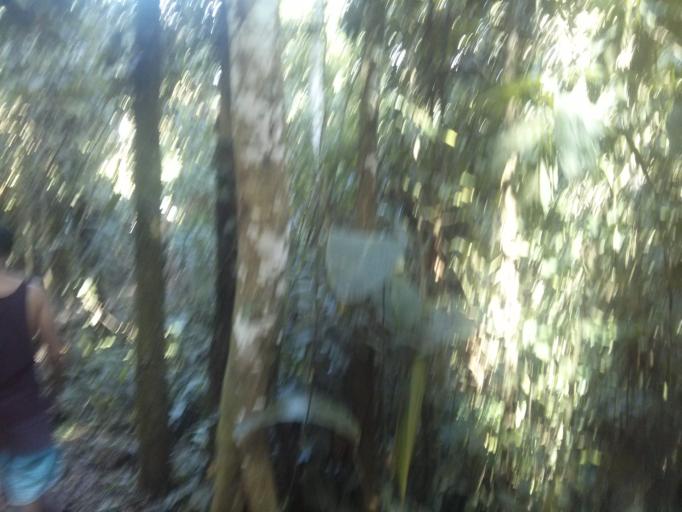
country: CR
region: Cartago
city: Turrialba
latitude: 9.9711
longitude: -83.6907
